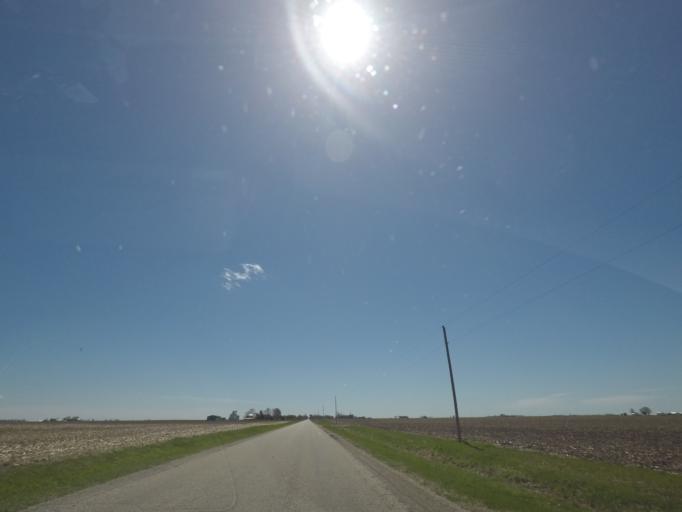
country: US
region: Illinois
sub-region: Logan County
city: Atlanta
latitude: 40.1640
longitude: -89.1936
